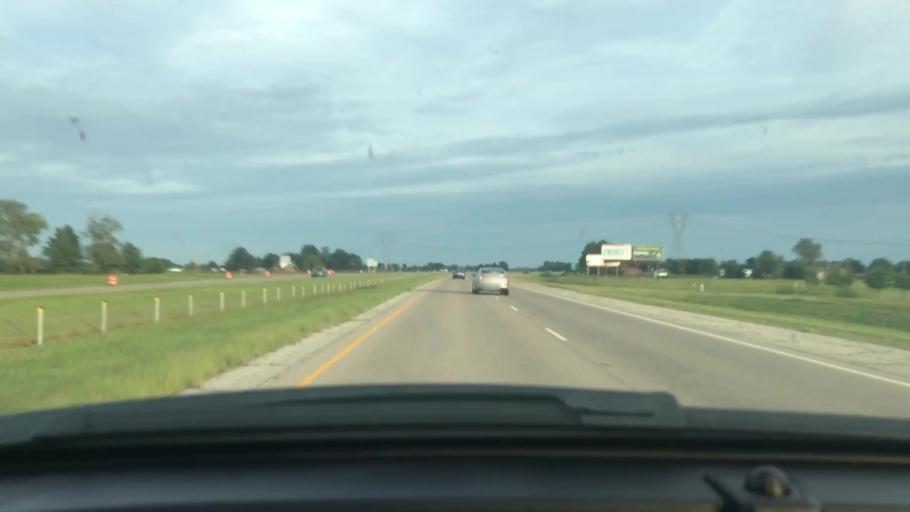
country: US
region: Arkansas
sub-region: Craighead County
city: Bay
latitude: 35.7736
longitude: -90.5832
